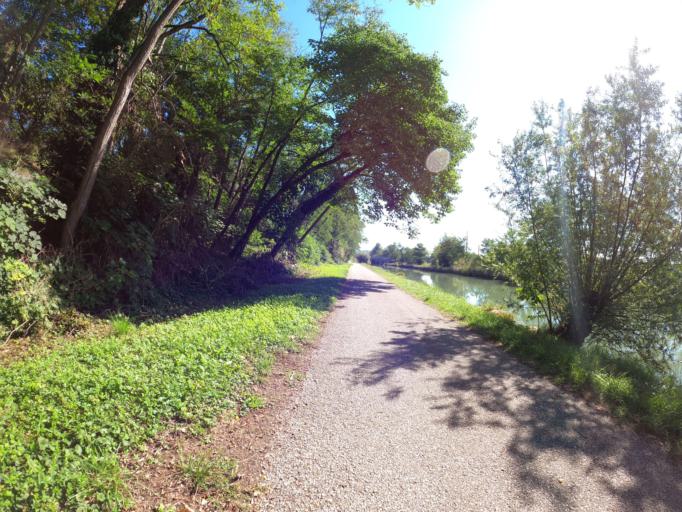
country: FR
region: Aquitaine
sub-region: Departement du Lot-et-Garonne
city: Castelculier
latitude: 44.1713
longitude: 0.6827
